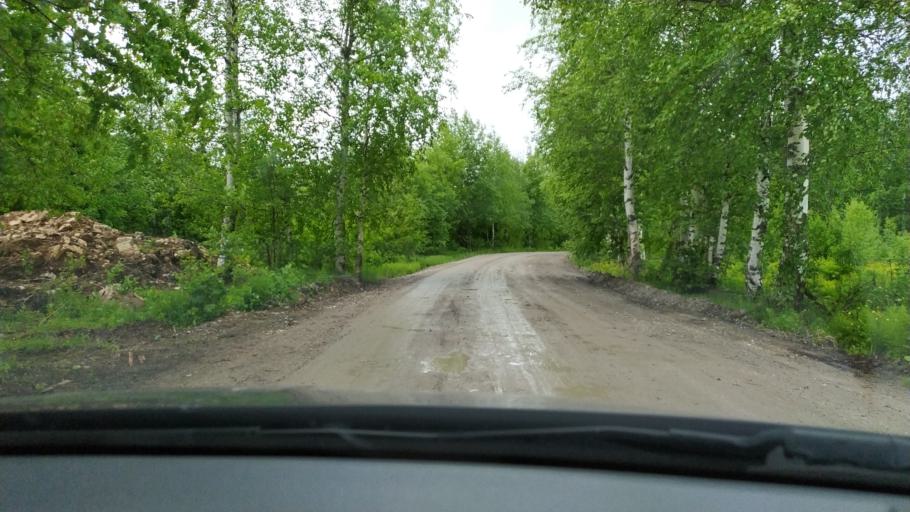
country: RU
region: Perm
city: Gremyachinsk
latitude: 58.5104
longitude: 57.8256
